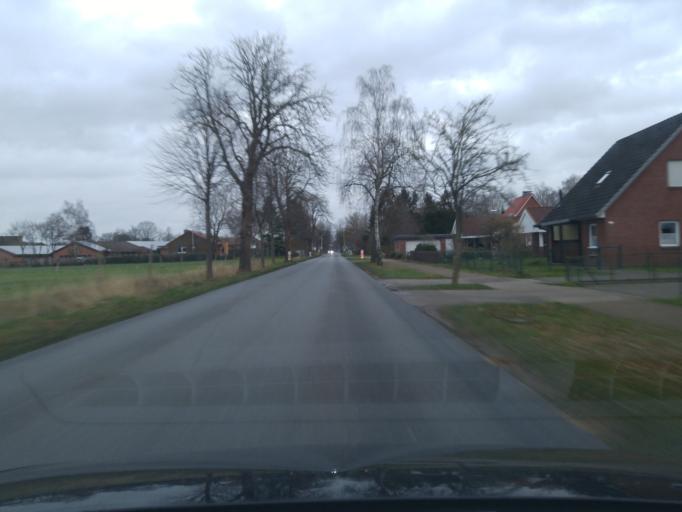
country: DE
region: Lower Saxony
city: Echem
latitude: 53.3386
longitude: 10.5362
